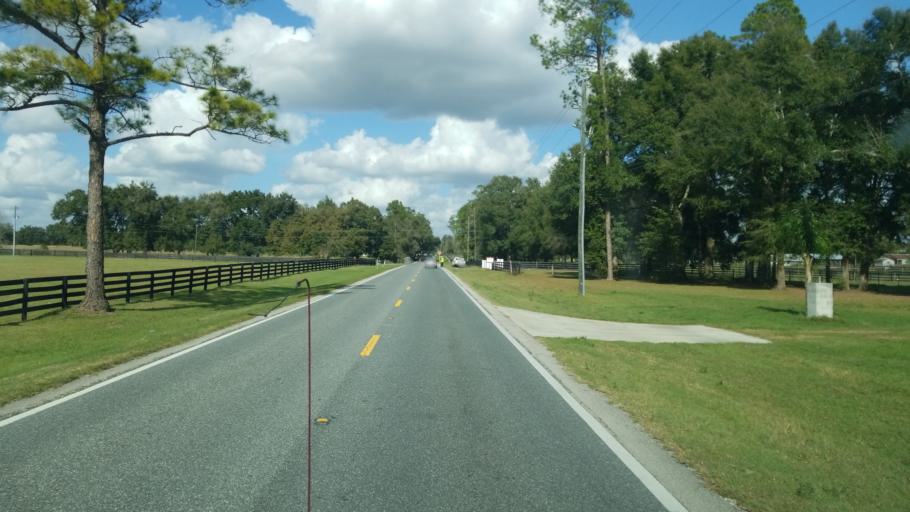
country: US
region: Florida
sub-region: Marion County
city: Belleview
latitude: 28.9986
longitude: -82.1199
